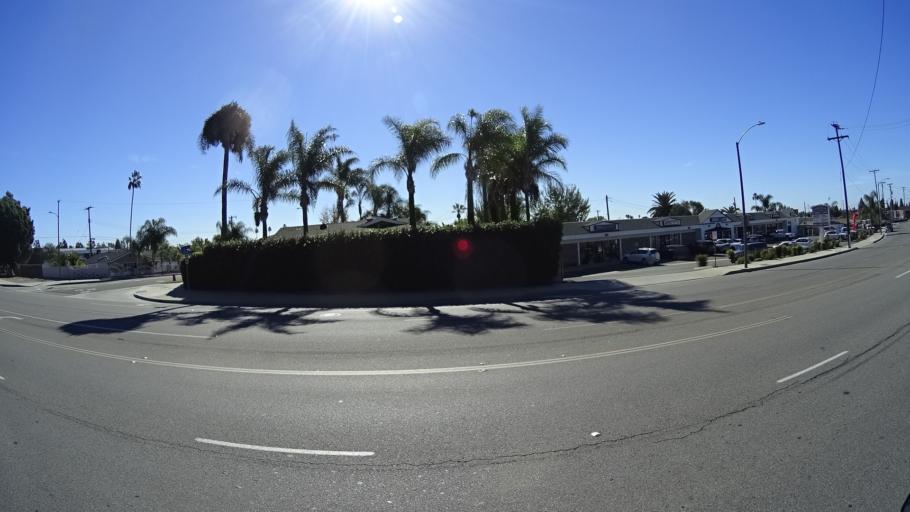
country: US
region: California
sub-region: Orange County
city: Villa Park
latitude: 33.8369
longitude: -117.8430
